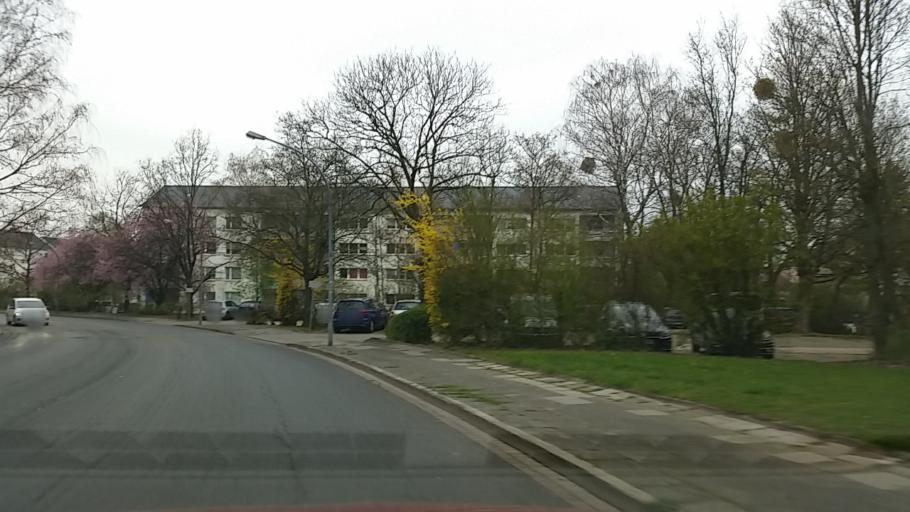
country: DE
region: Lower Saxony
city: Weyhausen
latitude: 52.4195
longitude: 10.7284
